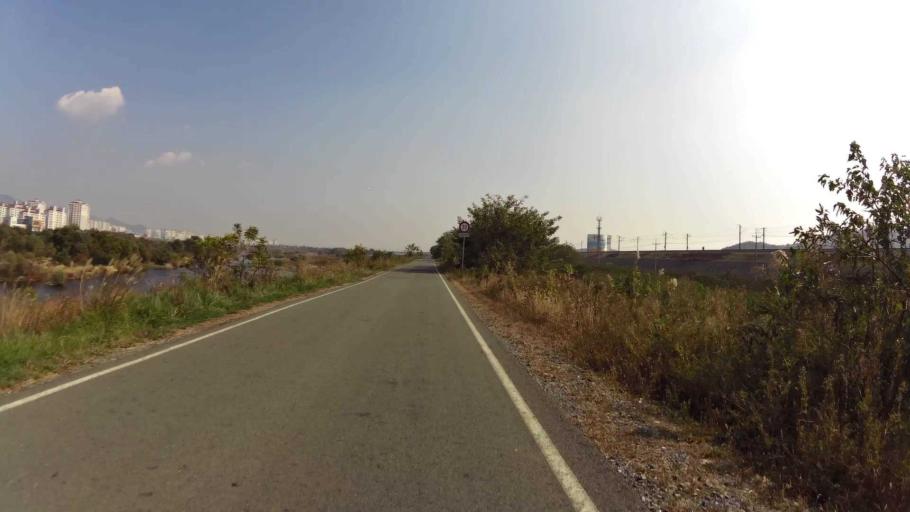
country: KR
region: Gyeongsangbuk-do
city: Gyeongsan-si
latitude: 35.8557
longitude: 128.6989
